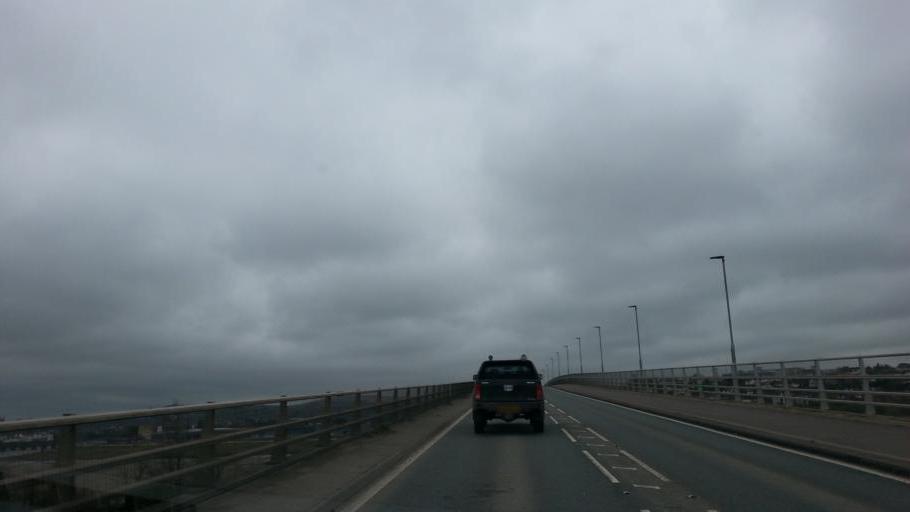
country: GB
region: England
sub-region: Devon
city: Barnstaple
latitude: 51.0813
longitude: -4.0722
